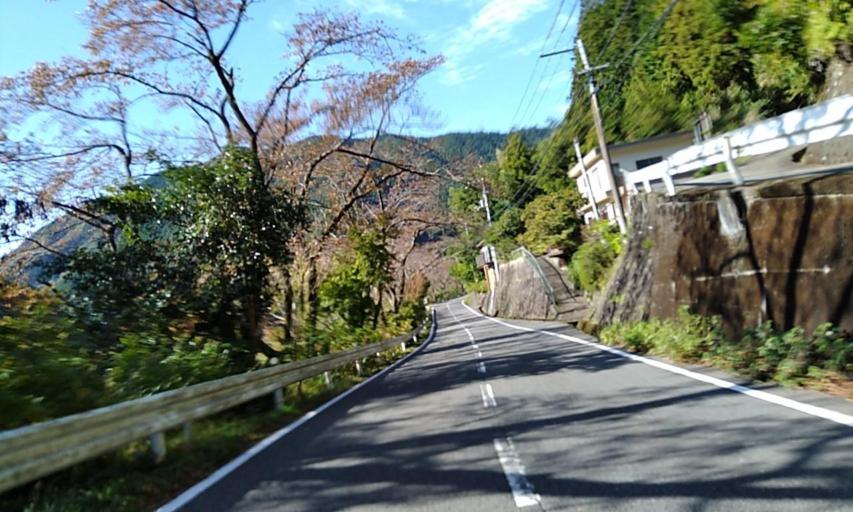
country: JP
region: Wakayama
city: Iwade
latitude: 34.0868
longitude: 135.3620
